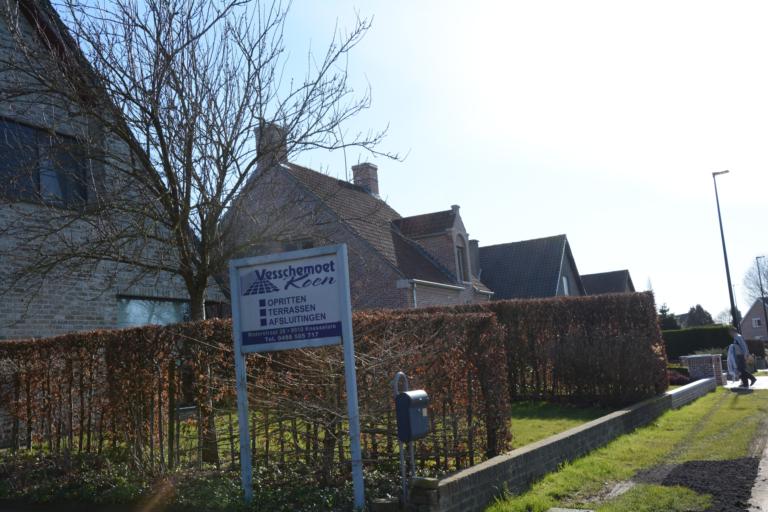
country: BE
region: Flanders
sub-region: Provincie Oost-Vlaanderen
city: Knesselare
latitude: 51.1453
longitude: 3.4313
